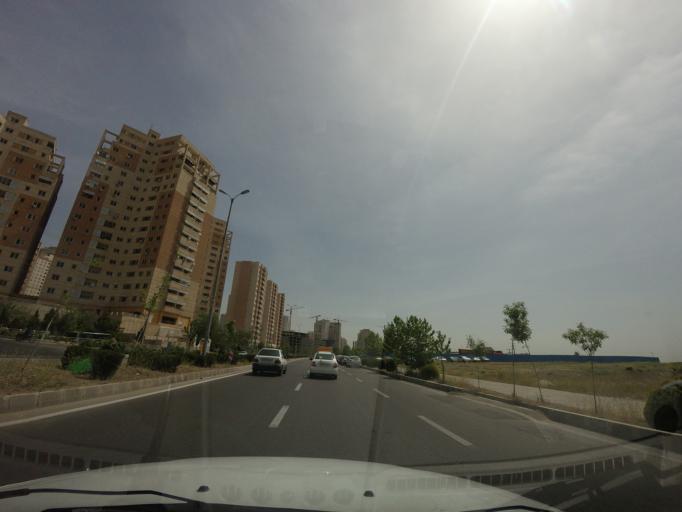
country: IR
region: Tehran
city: Shahr-e Qods
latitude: 35.7535
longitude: 51.2044
